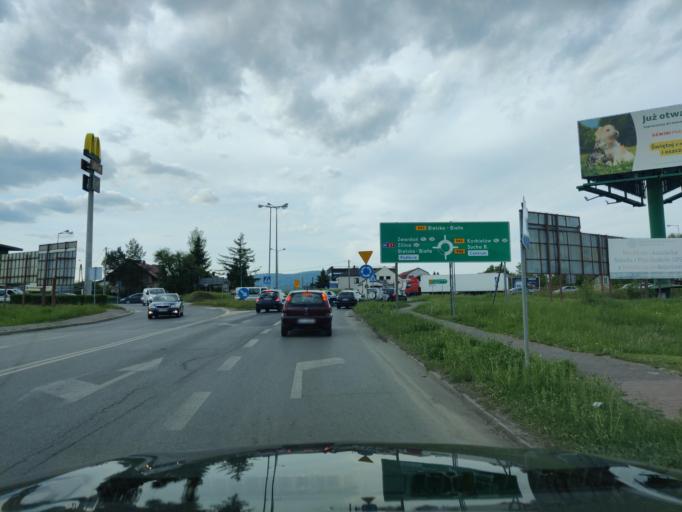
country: PL
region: Silesian Voivodeship
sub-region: Powiat zywiecki
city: Zywiec
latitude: 49.6904
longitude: 19.1824
